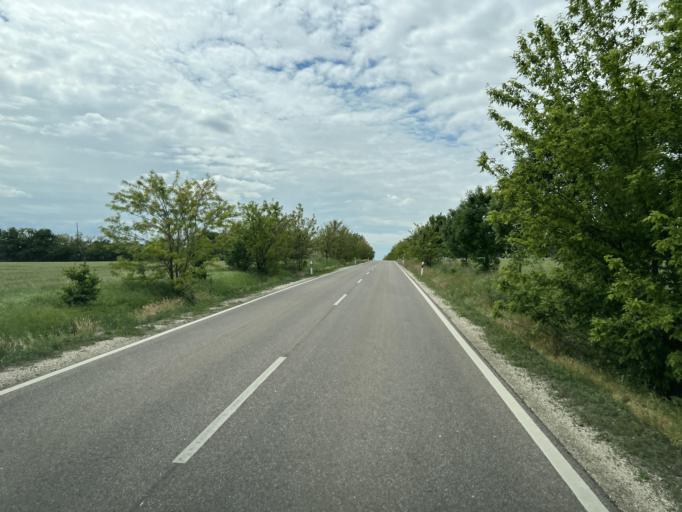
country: HU
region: Pest
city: Zsambok
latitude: 47.5302
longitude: 19.6020
